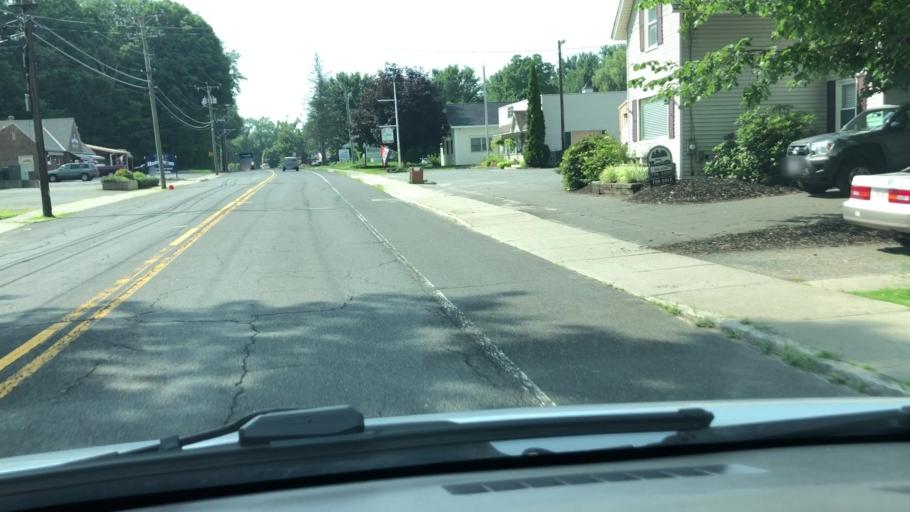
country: US
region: Massachusetts
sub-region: Franklin County
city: Greenfield
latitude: 42.5763
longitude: -72.5976
